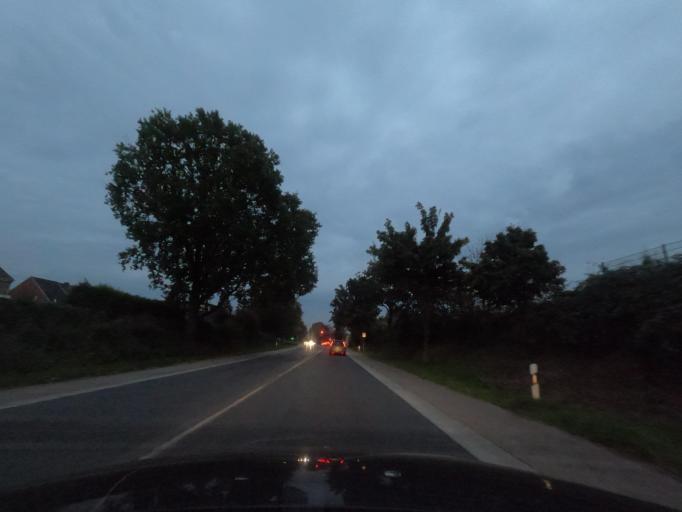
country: DE
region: North Rhine-Westphalia
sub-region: Regierungsbezirk Dusseldorf
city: Wesel
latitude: 51.6764
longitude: 6.6275
